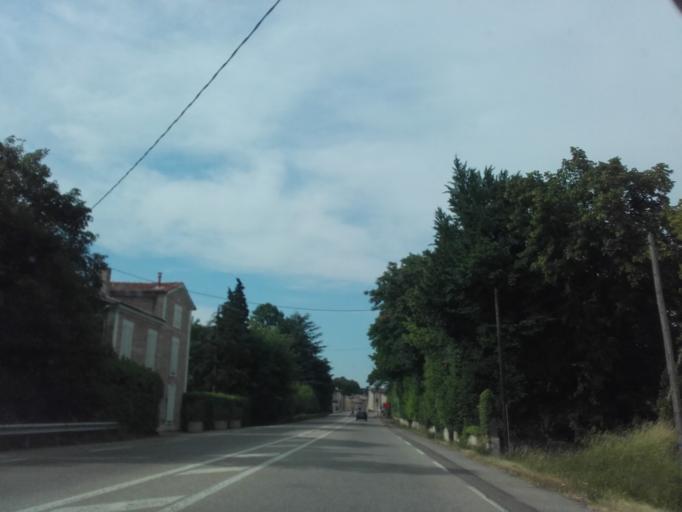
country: FR
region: Rhone-Alpes
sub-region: Departement de la Drome
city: Saulce-sur-Rhone
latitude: 44.7002
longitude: 4.7990
